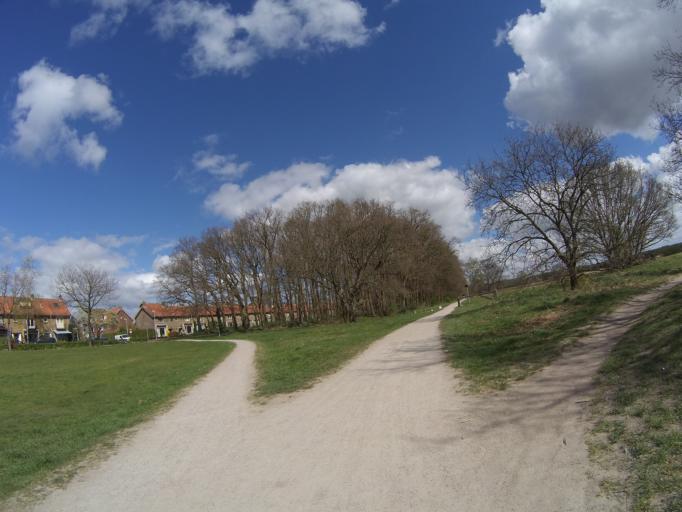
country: NL
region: North Holland
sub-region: Gemeente Bussum
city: Bussum
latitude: 52.2616
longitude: 5.1739
